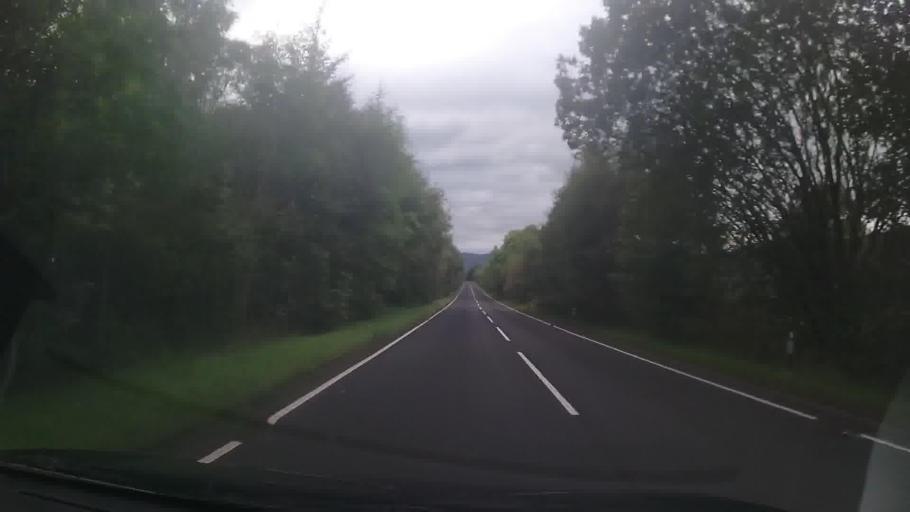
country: GB
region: Scotland
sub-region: Argyll and Bute
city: Garelochhead
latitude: 56.2294
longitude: -4.9991
